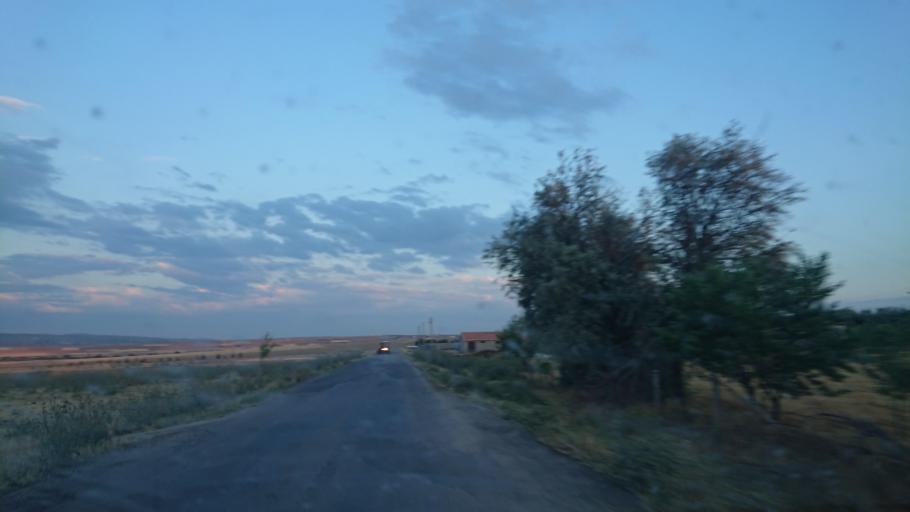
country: TR
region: Aksaray
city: Balci
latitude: 38.8269
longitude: 34.0974
